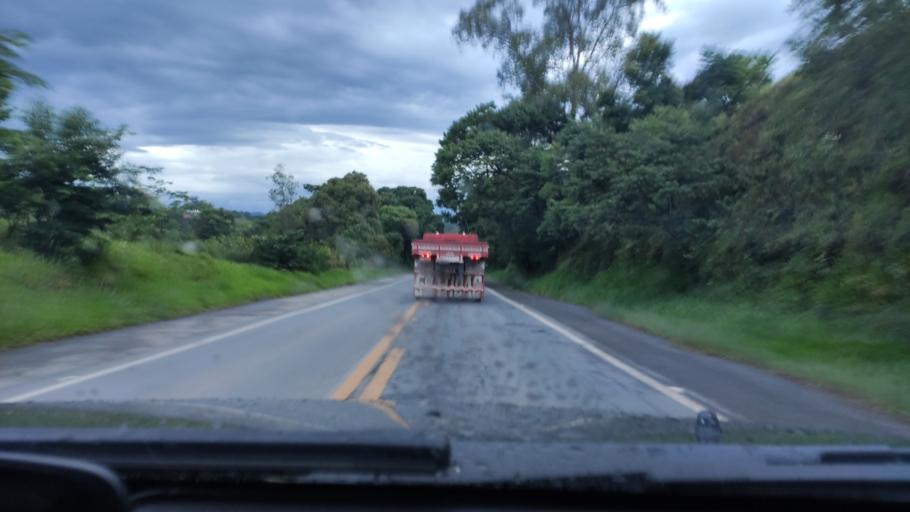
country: BR
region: Sao Paulo
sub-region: Socorro
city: Socorro
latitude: -22.7435
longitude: -46.5635
